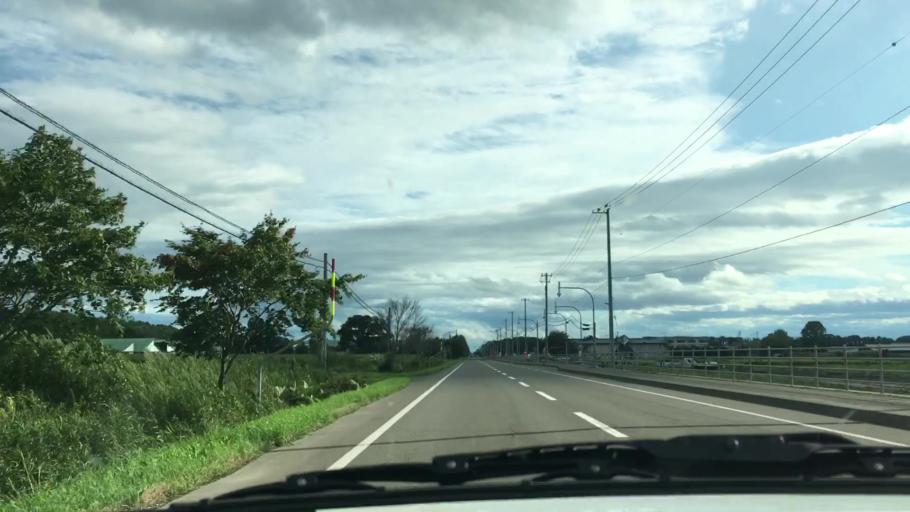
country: JP
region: Hokkaido
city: Otofuke
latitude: 43.2559
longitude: 143.3003
